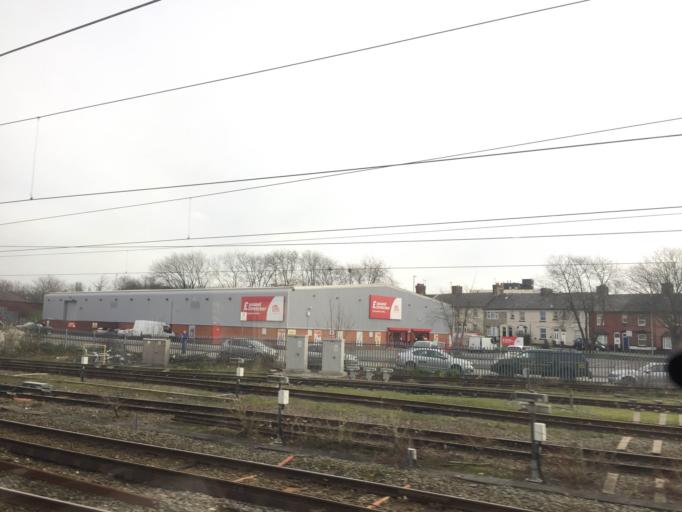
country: GB
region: England
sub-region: Warrington
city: Warrington
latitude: 53.3875
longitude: -2.6035
